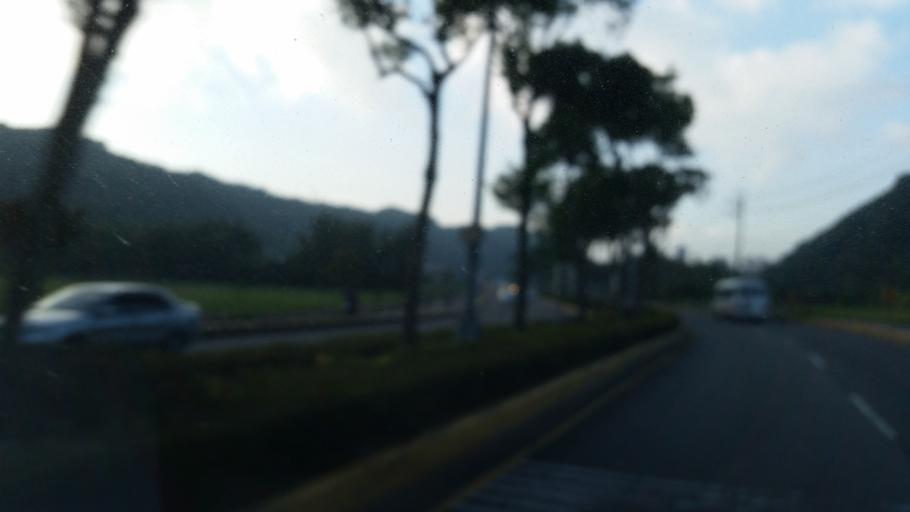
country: TW
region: Taiwan
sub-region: Taoyuan
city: Taoyuan
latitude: 25.0181
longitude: 121.3486
